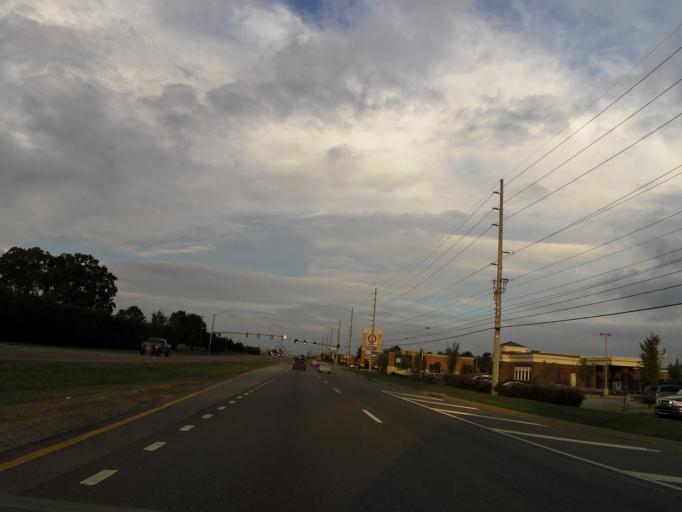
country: US
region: Alabama
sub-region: Madison County
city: Madison
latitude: 34.7508
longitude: -86.7568
